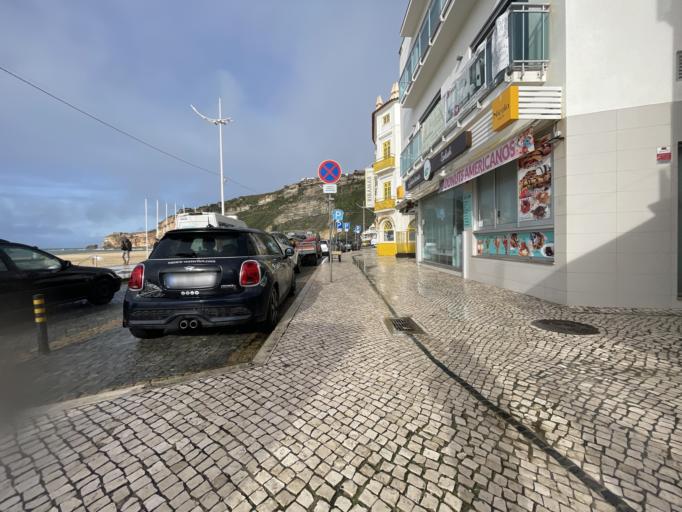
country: PT
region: Leiria
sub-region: Nazare
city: Nazare
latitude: 39.6012
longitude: -9.0736
